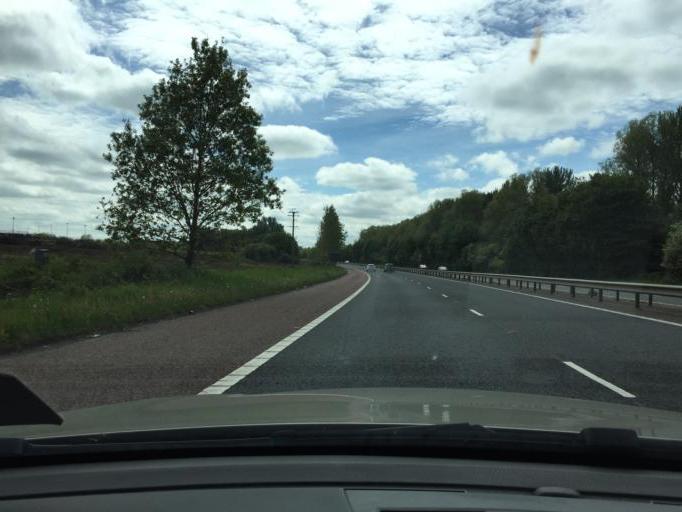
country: GB
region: Northern Ireland
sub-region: Craigavon District
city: Craigavon
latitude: 54.4593
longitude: -6.4224
